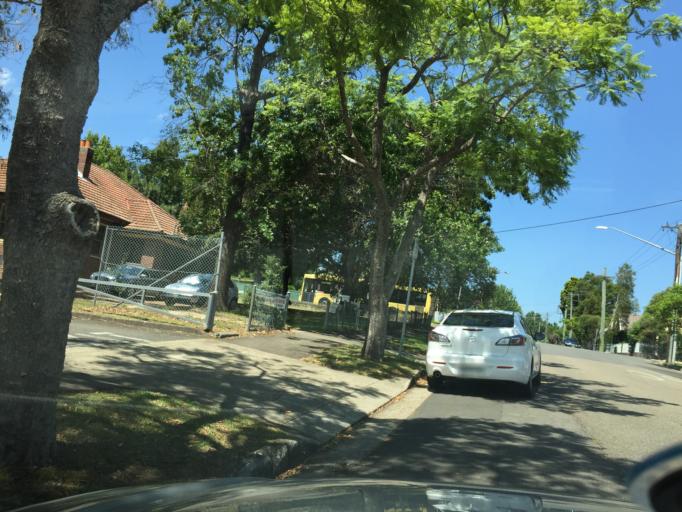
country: AU
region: New South Wales
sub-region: Parramatta
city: City of Parramatta
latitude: -33.8051
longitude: 151.0020
